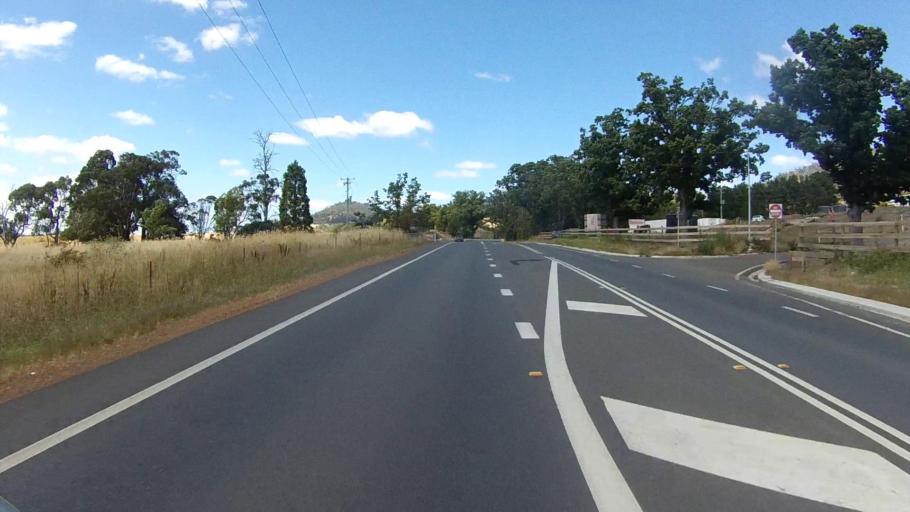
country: AU
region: Tasmania
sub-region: Clarence
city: Cambridge
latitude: -42.8030
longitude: 147.4228
